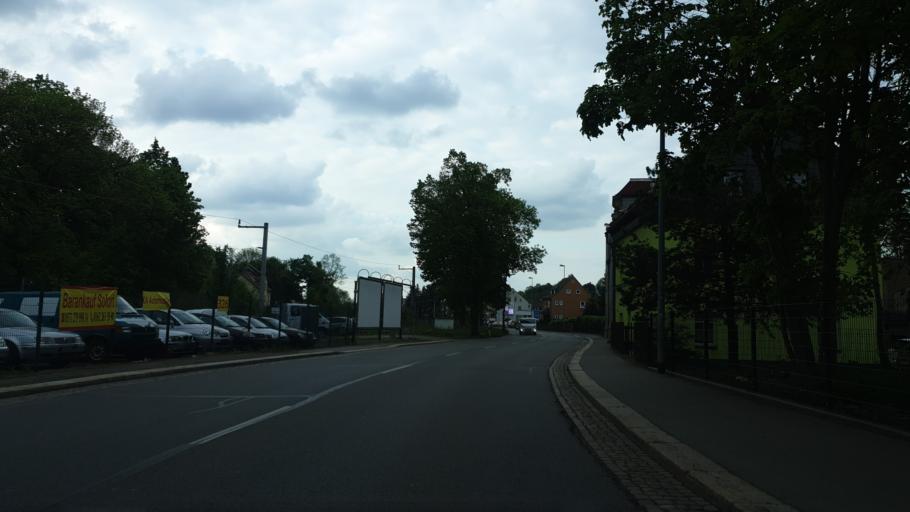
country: DE
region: Saxony
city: Burkhardtsdorf
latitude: 50.7833
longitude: 12.9249
